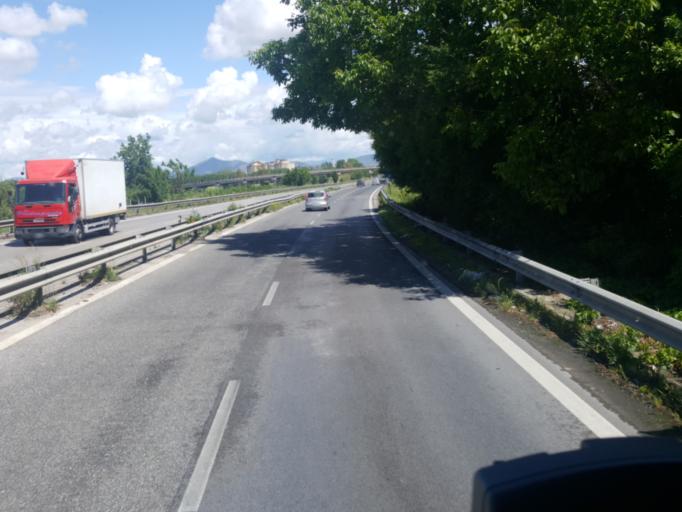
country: IT
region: Campania
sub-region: Provincia di Napoli
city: Pascarola
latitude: 40.9877
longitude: 14.2925
